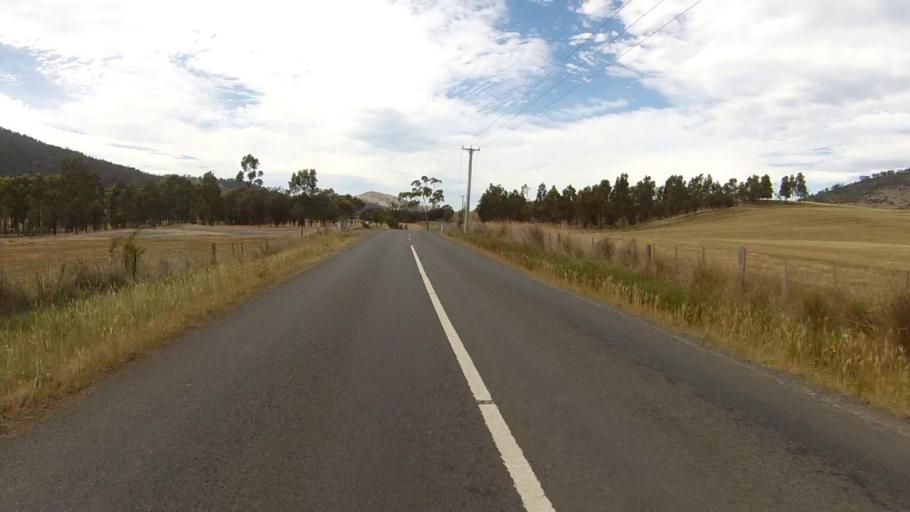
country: AU
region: Tasmania
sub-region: Brighton
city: Old Beach
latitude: -42.7159
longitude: 147.3843
